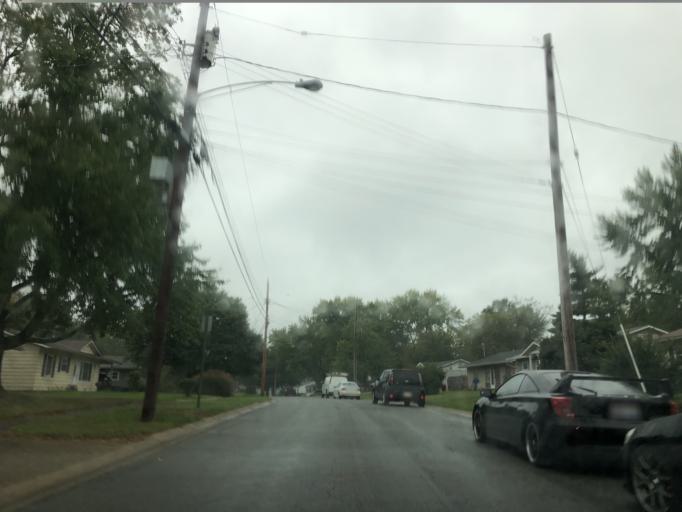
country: US
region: Ohio
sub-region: Hamilton County
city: Loveland
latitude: 39.2659
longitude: -84.2730
